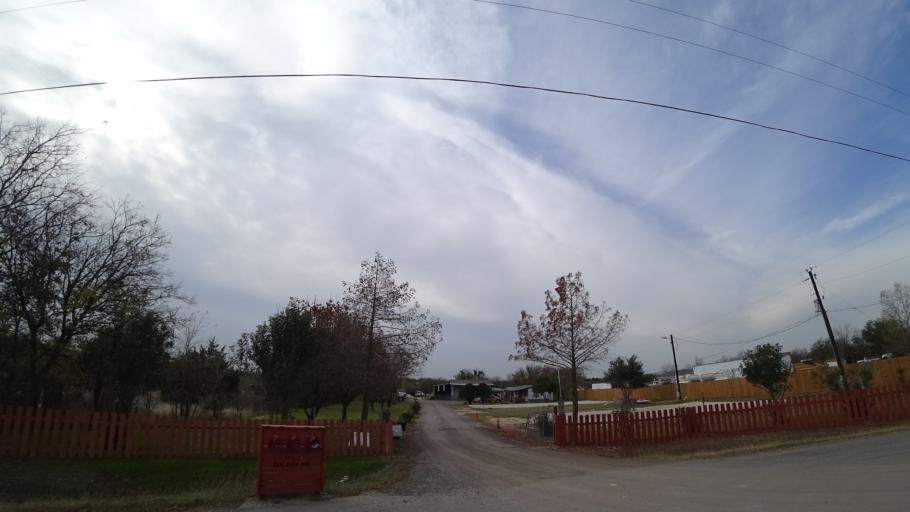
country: US
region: Texas
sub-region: Travis County
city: Garfield
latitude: 30.1469
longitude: -97.6663
